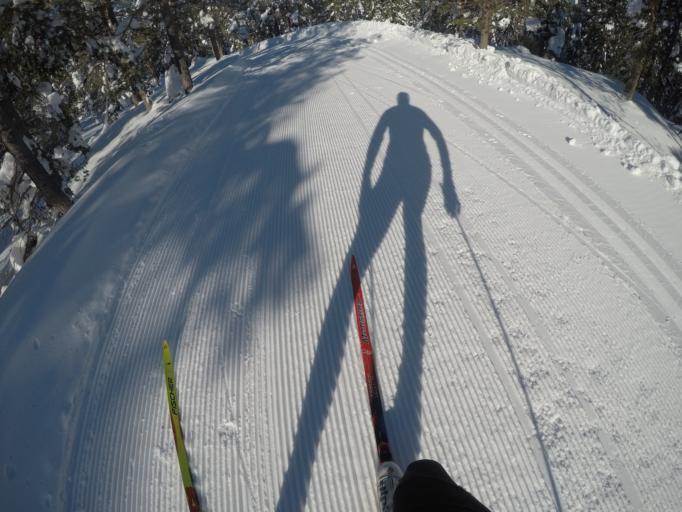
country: SE
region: Vaesternorrland
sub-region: Sundsvalls Kommun
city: Sundsvall
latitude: 62.3663
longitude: 17.3039
